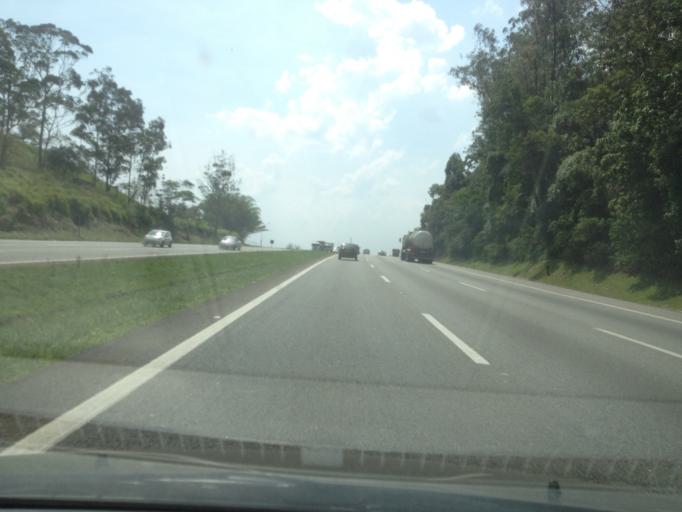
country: BR
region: Sao Paulo
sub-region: Itapevi
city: Itapevi
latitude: -23.5045
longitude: -46.9797
